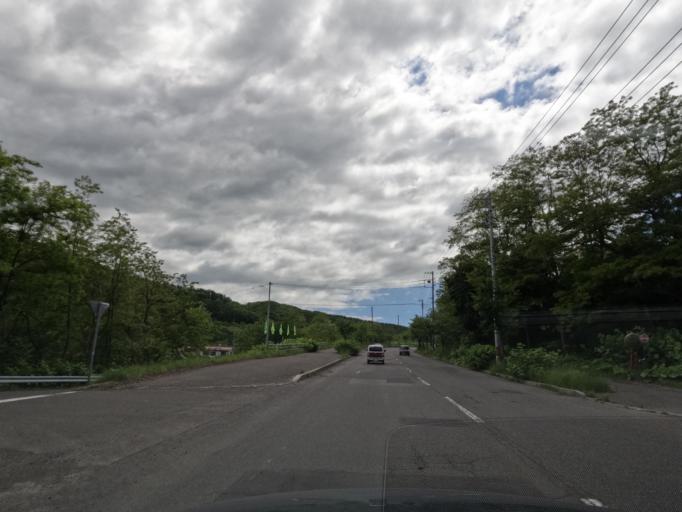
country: JP
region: Hokkaido
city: Bibai
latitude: 43.2580
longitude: 141.9437
